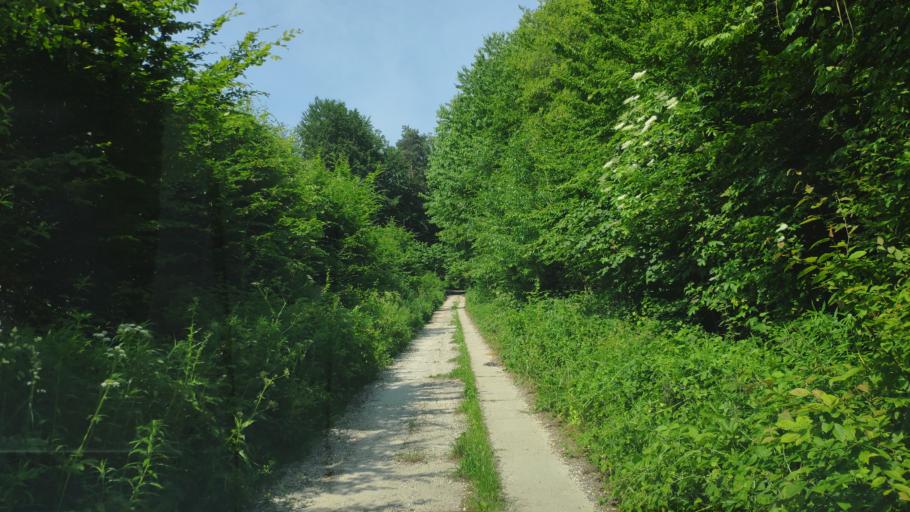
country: SK
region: Presovsky
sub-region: Okres Presov
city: Presov
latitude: 48.9704
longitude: 21.1461
